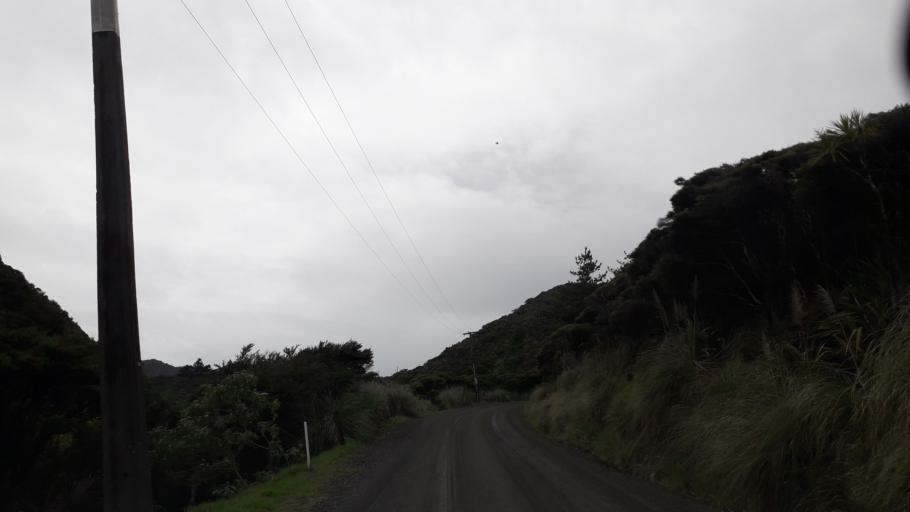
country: NZ
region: Northland
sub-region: Far North District
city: Ahipara
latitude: -35.4406
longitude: 173.3007
